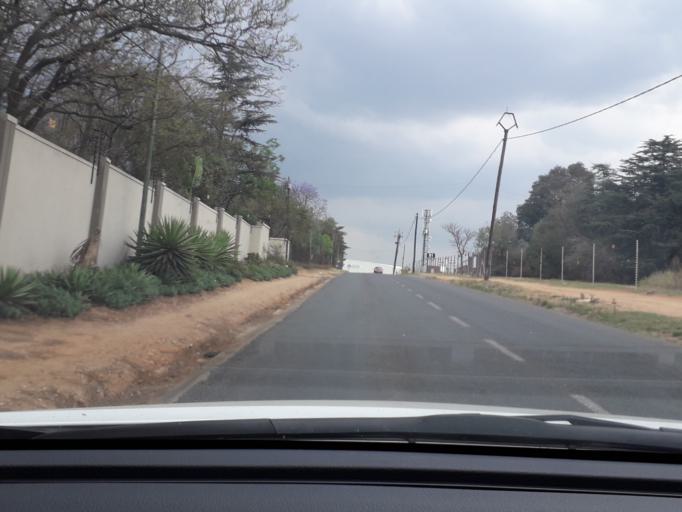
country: ZA
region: Gauteng
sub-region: West Rand District Municipality
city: Muldersdriseloop
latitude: -26.0695
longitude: 27.9237
